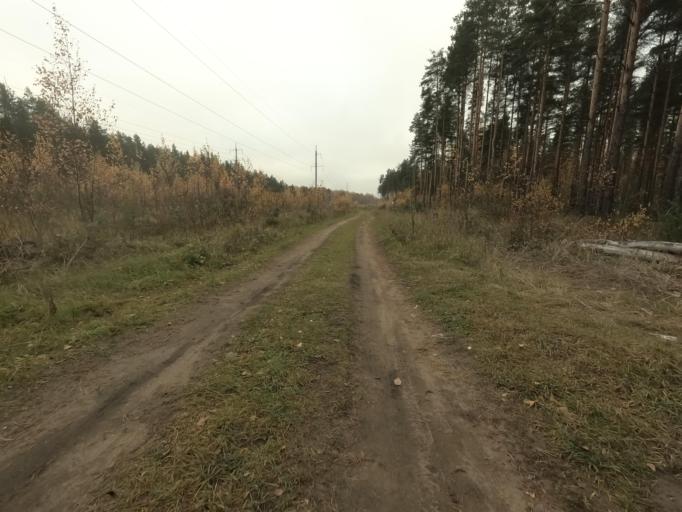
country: RU
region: Leningrad
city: Kirovsk
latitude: 59.8508
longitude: 30.9836
